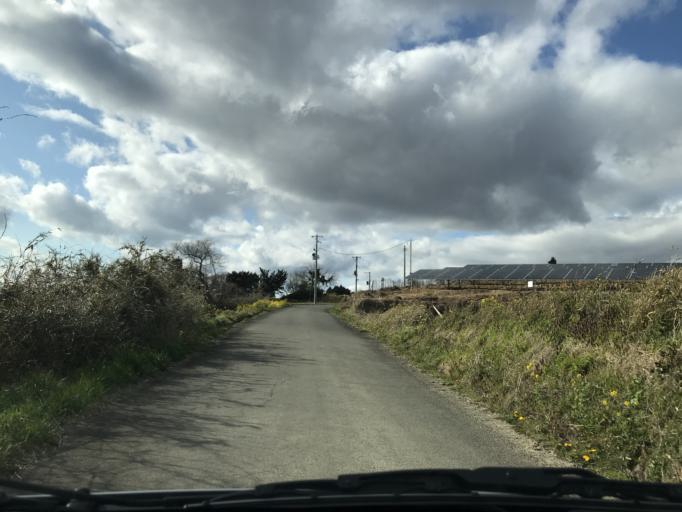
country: JP
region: Miyagi
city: Wakuya
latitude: 38.6157
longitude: 141.2304
